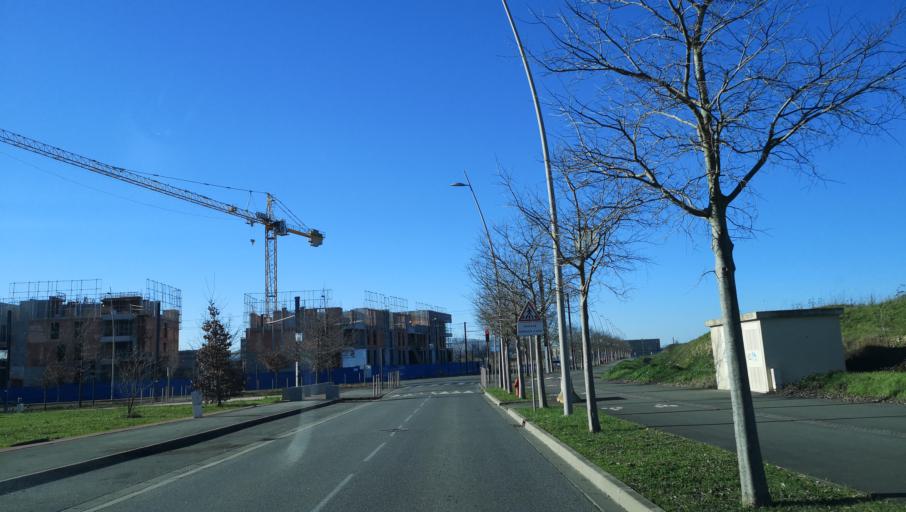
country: FR
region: Midi-Pyrenees
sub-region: Departement de la Haute-Garonne
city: Beauzelle
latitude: 43.6628
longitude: 1.3686
